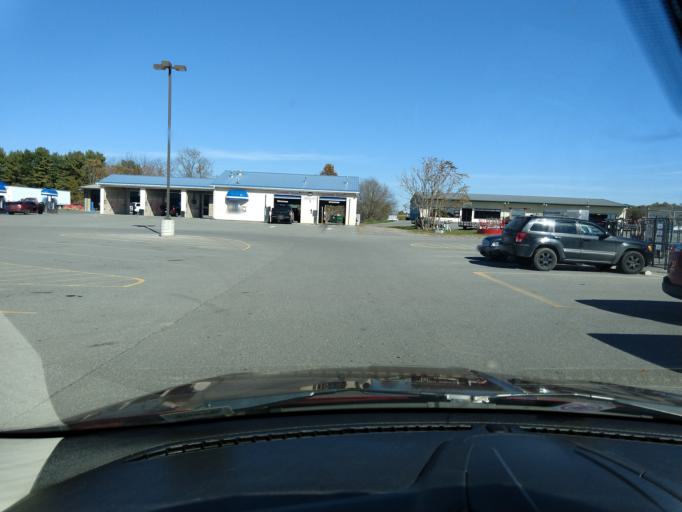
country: US
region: West Virginia
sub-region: Greenbrier County
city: Ronceverte
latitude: 37.7653
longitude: -80.4650
